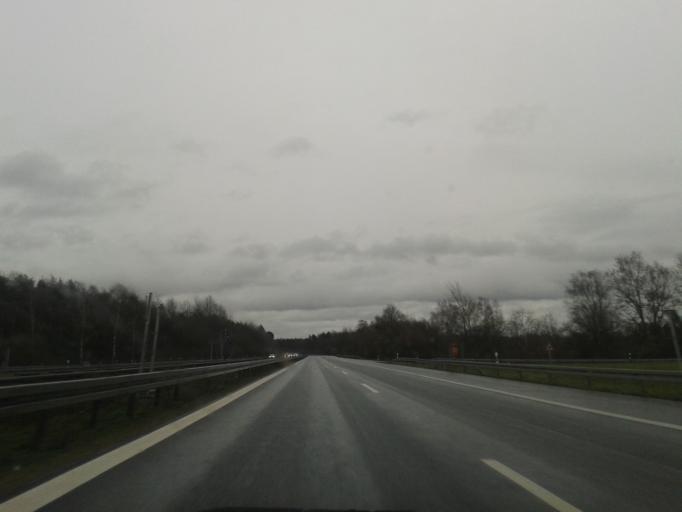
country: DE
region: Saxony
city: Lichtenberg
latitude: 51.1572
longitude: 13.9763
